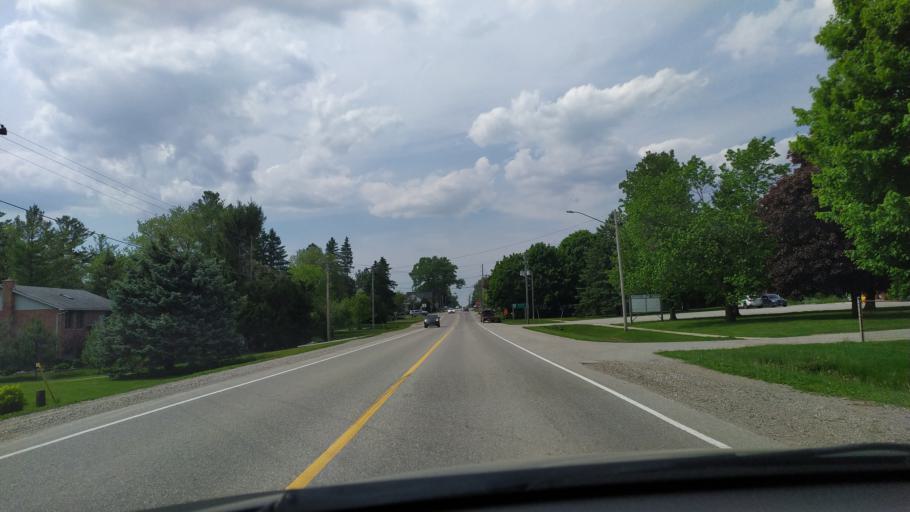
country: CA
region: Ontario
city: Dorchester
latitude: 43.1373
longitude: -81.0293
